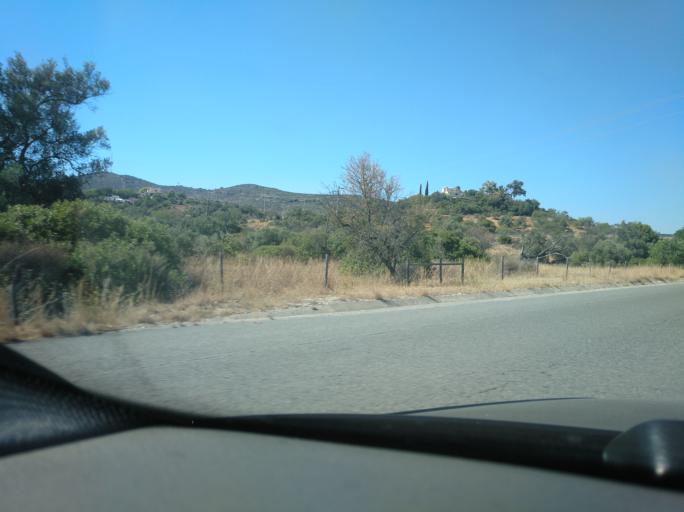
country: PT
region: Faro
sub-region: Olhao
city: Moncarapacho
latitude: 37.0875
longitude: -7.8032
